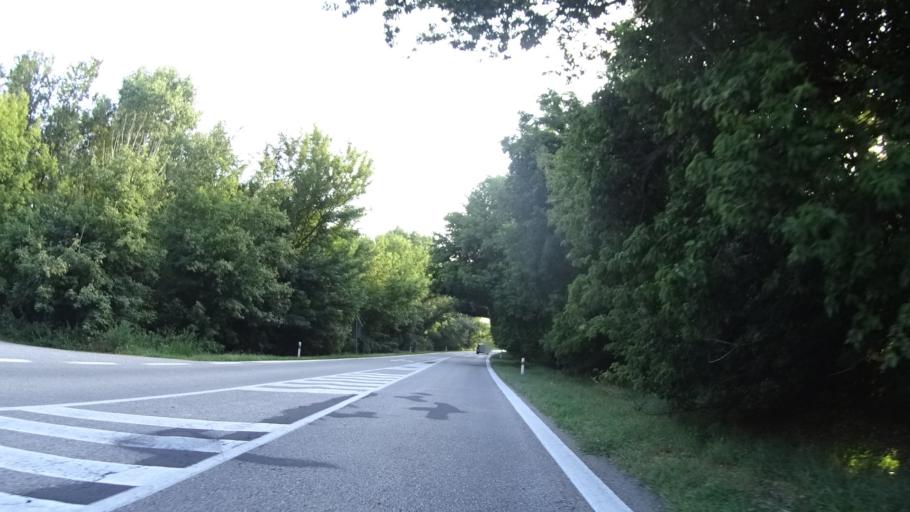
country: HU
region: Komarom-Esztergom
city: Nyergesujfalu
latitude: 47.7668
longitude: 18.5336
